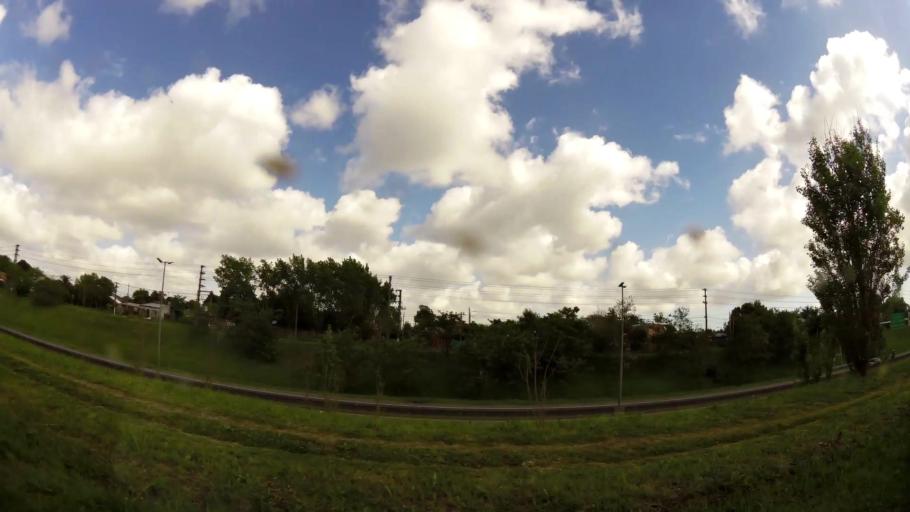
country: AR
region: Buenos Aires
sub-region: Partido de Quilmes
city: Quilmes
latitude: -34.8167
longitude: -58.1828
